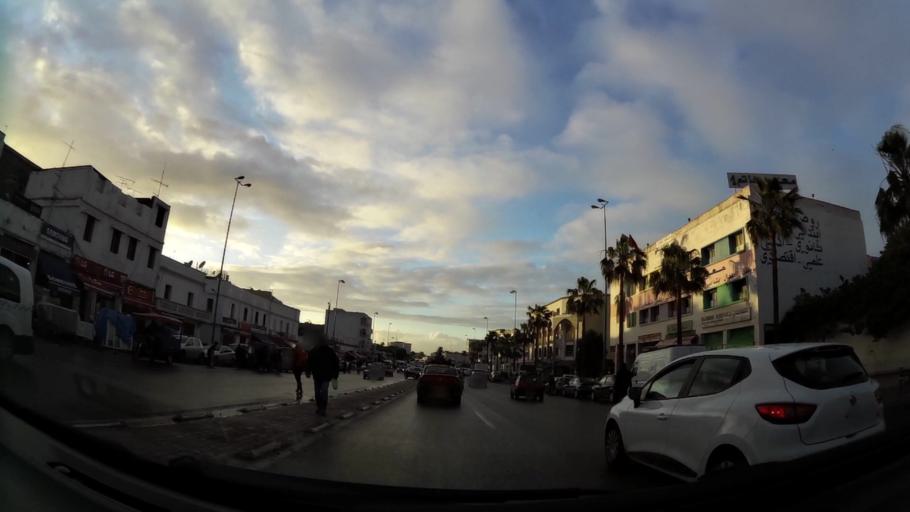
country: MA
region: Grand Casablanca
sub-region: Casablanca
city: Casablanca
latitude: 33.5777
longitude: -7.6000
